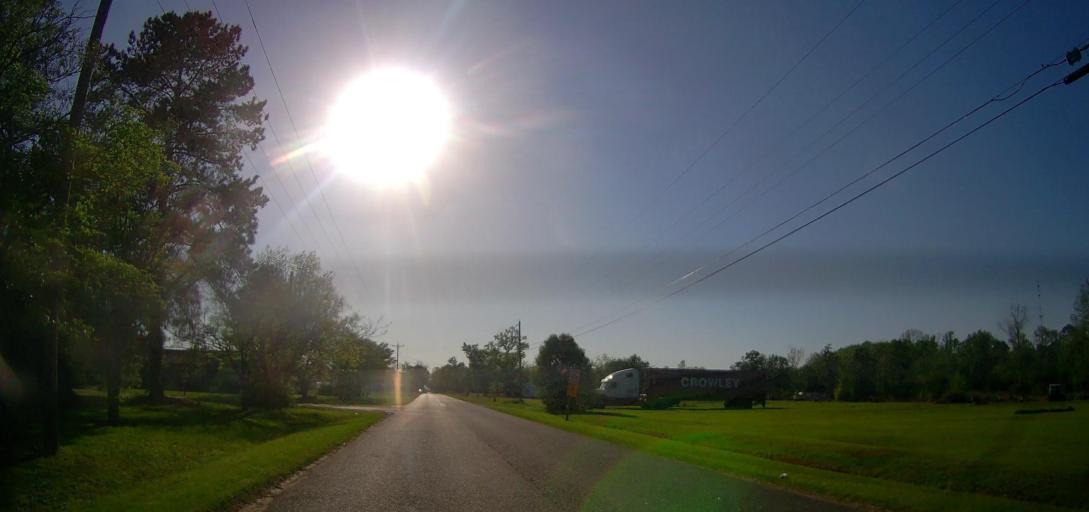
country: US
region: Georgia
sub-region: Ben Hill County
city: Fitzgerald
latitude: 31.7289
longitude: -83.2696
